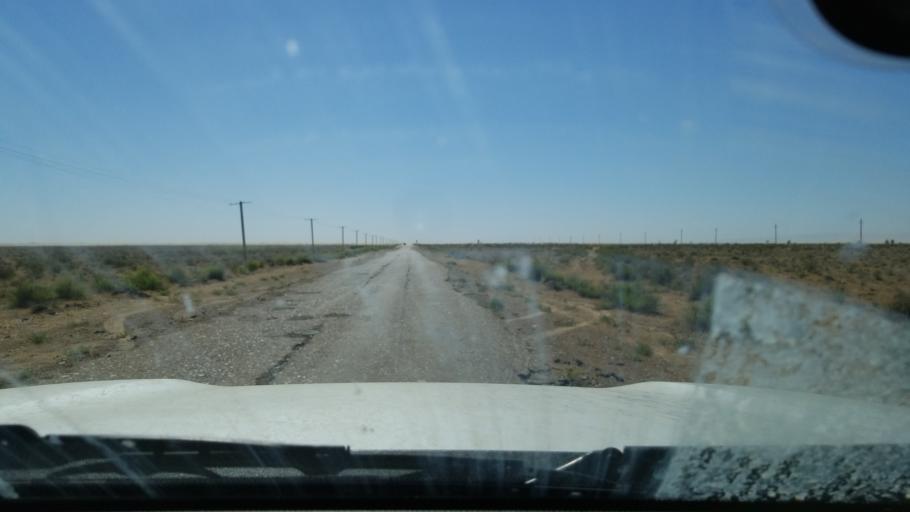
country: TM
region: Balkan
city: Balkanabat
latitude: 40.1661
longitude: 54.3122
